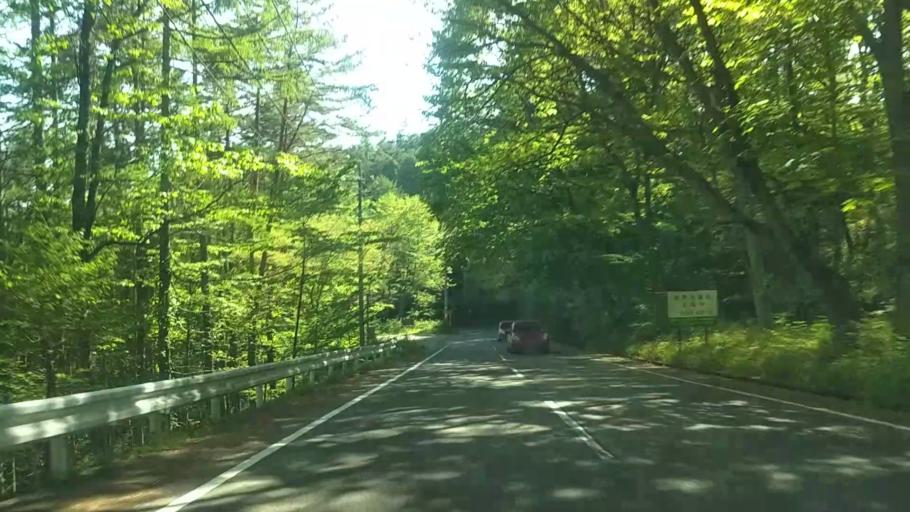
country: JP
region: Yamanashi
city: Nirasaki
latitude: 35.8876
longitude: 138.3893
